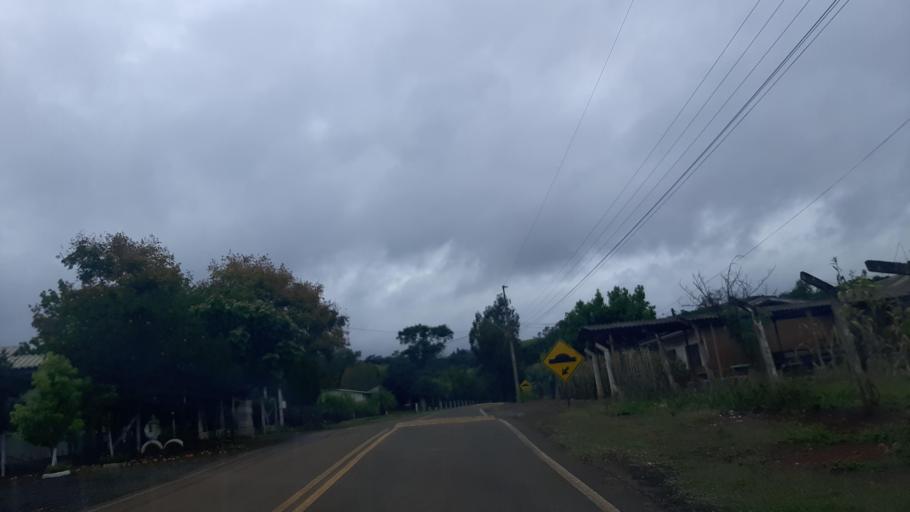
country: BR
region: Parana
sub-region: Ampere
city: Ampere
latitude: -25.9762
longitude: -53.4437
